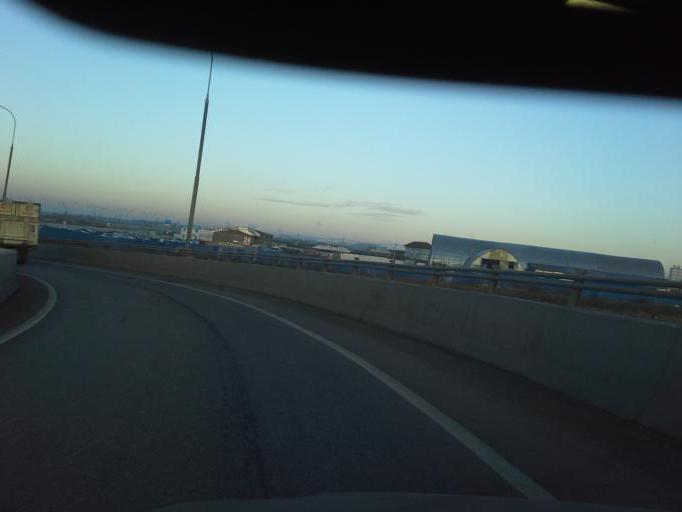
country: RU
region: Moscow
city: Vnukovo
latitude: 55.5857
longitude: 37.2133
